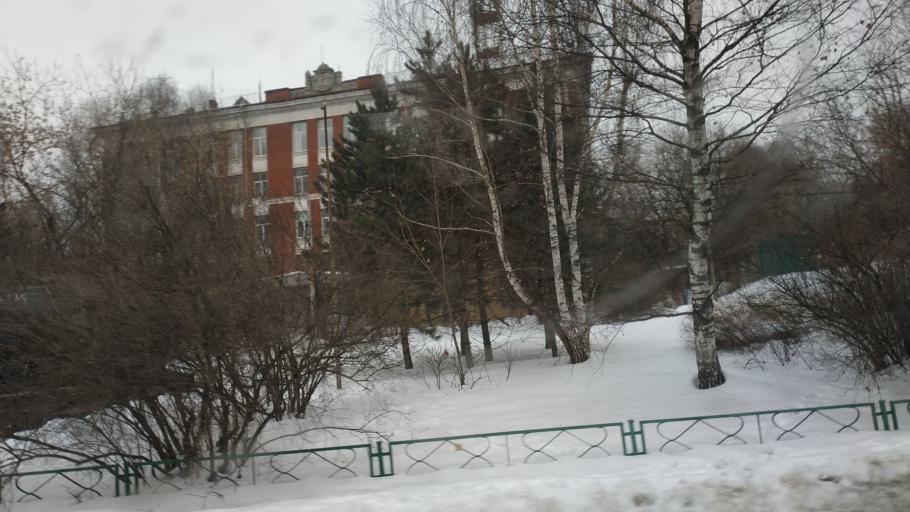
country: RU
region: Moscow
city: Shchukino
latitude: 55.7810
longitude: 37.4389
